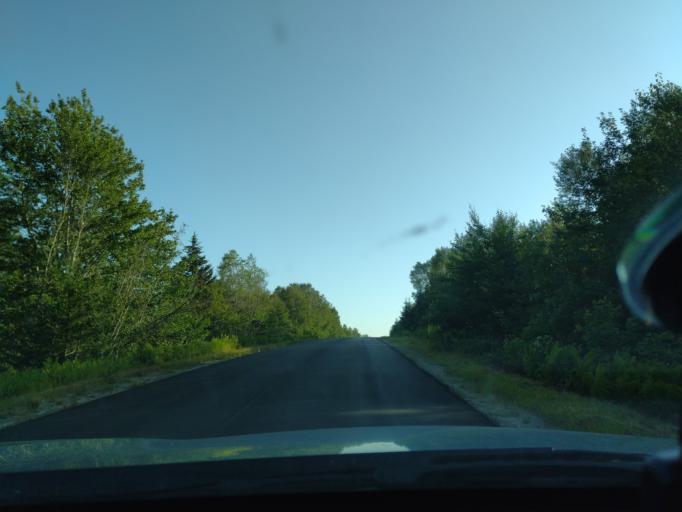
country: US
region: Maine
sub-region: Washington County
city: Eastport
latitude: 44.7141
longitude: -67.1389
